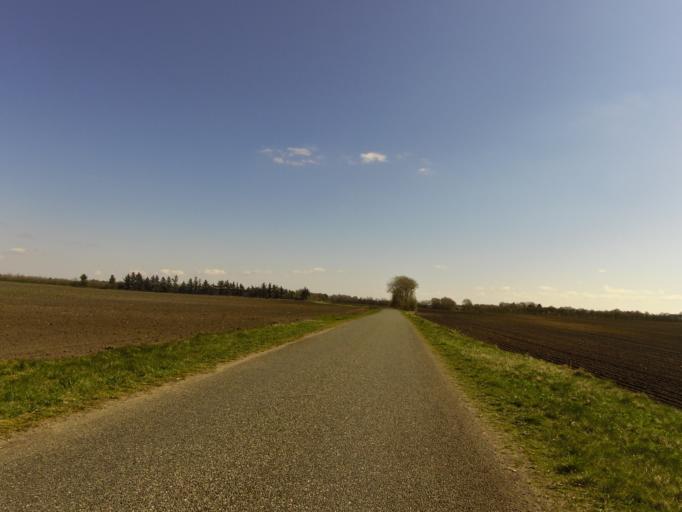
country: DK
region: South Denmark
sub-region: Esbjerg Kommune
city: Ribe
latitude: 55.3386
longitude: 8.8691
